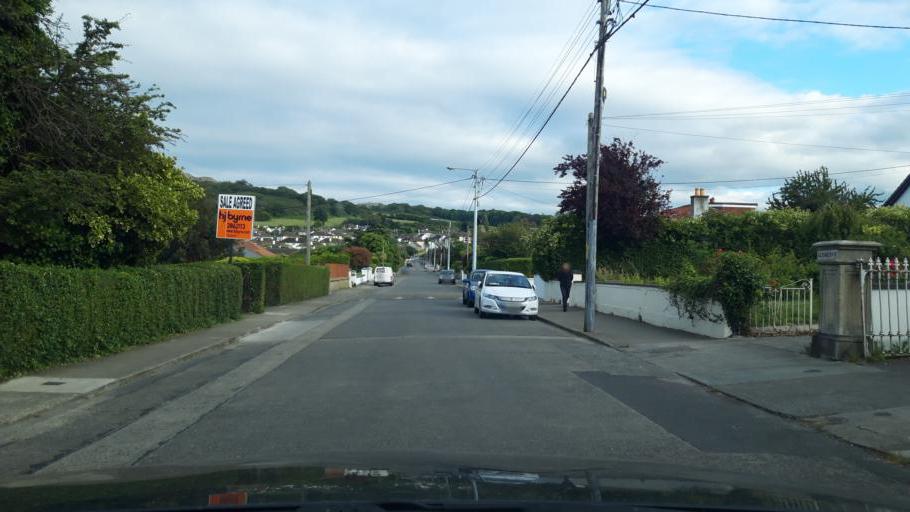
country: IE
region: Leinster
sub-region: Wicklow
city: Bray
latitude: 53.1980
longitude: -6.1005
